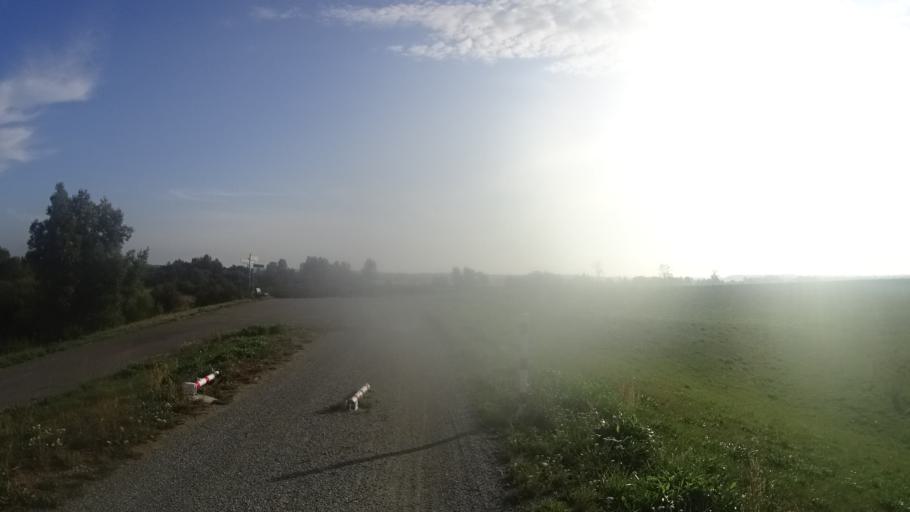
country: DE
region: Brandenburg
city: Lanz
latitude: 53.0577
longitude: 11.5522
